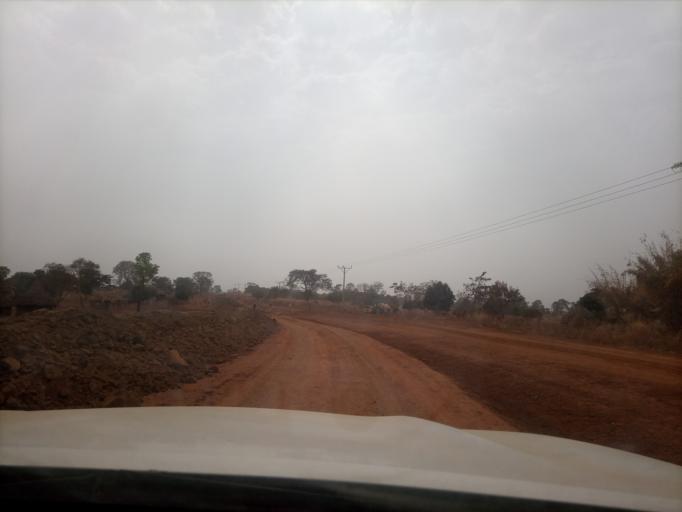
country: ET
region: Oromiya
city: Mendi
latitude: 10.1291
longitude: 35.1302
